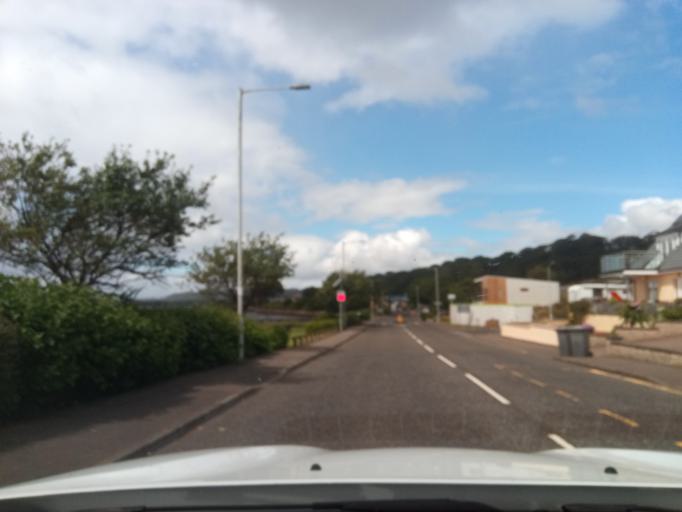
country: GB
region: Scotland
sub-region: Fife
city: Oakley
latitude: 56.0583
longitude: -3.5728
